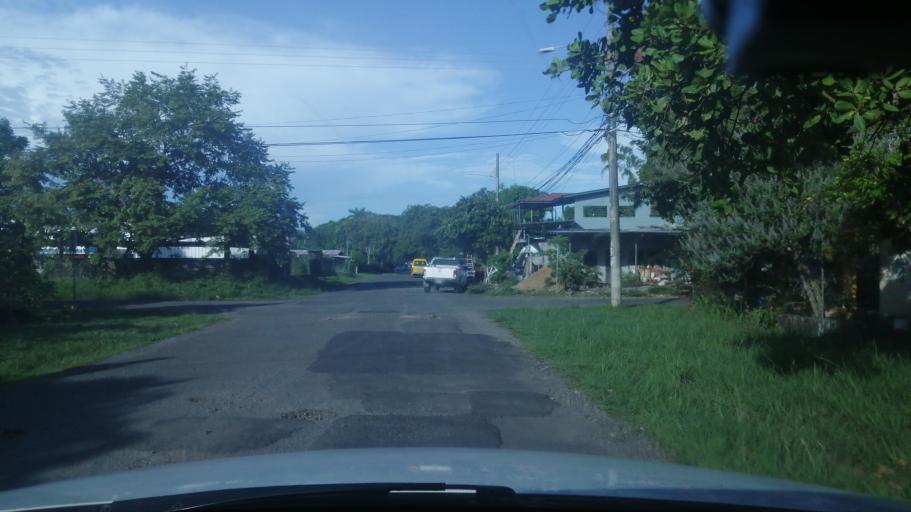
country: PA
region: Chiriqui
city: David
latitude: 8.4332
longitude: -82.4359
